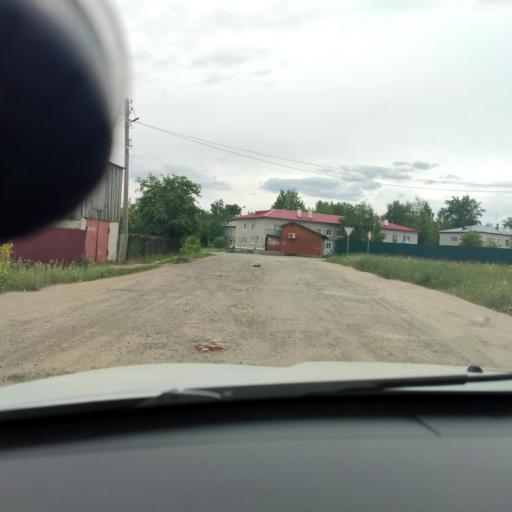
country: RU
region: Perm
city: Polazna
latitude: 58.2999
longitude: 56.4013
